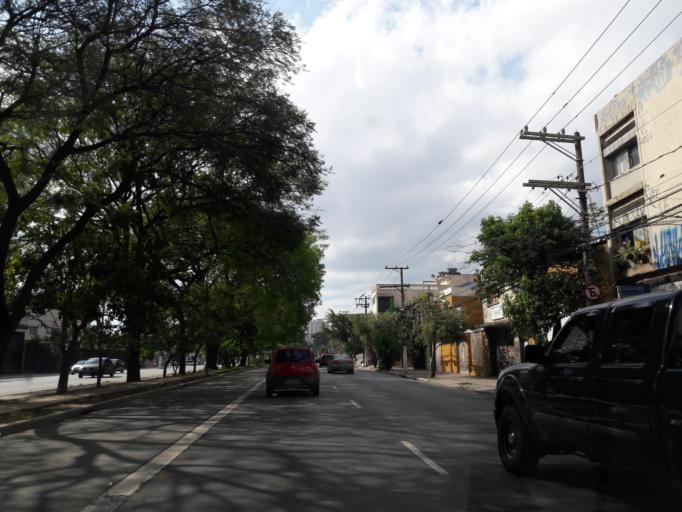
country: BR
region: Sao Paulo
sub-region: Sao Paulo
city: Sao Paulo
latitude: -23.5207
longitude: -46.6519
